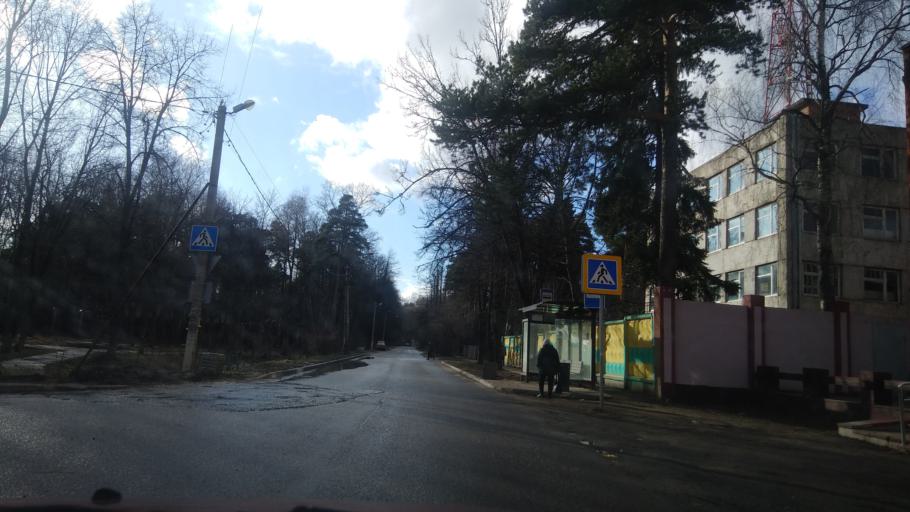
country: RU
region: Moskovskaya
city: Mamontovka
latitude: 56.0104
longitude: 37.8317
